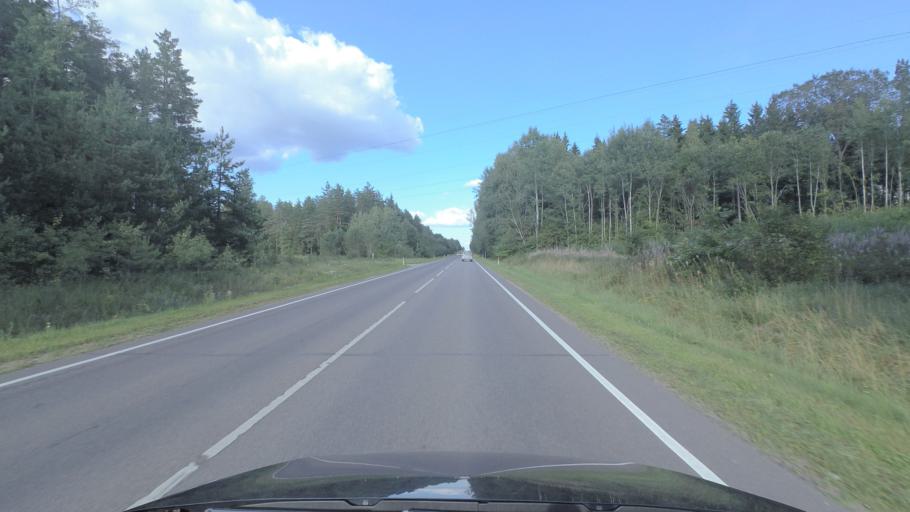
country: LT
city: Pabrade
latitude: 54.9710
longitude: 25.7295
